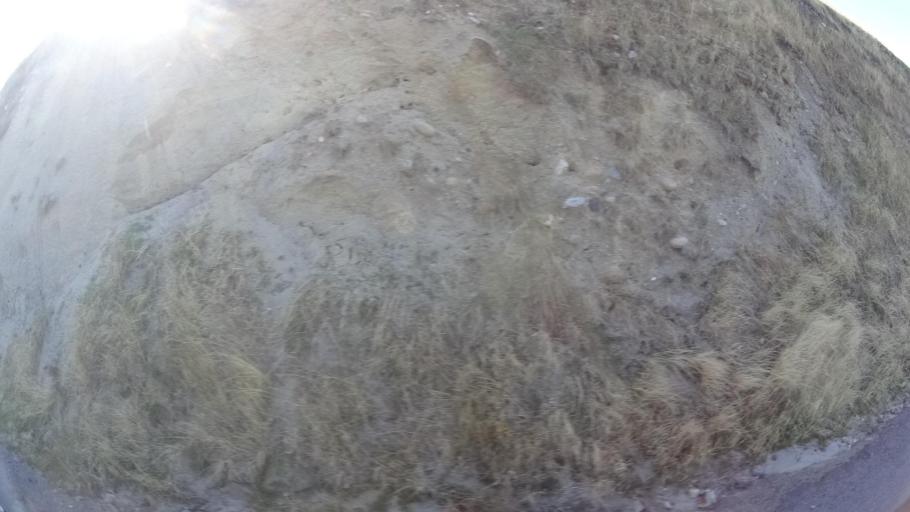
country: US
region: California
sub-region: Kern County
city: Lamont
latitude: 35.4010
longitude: -118.7823
